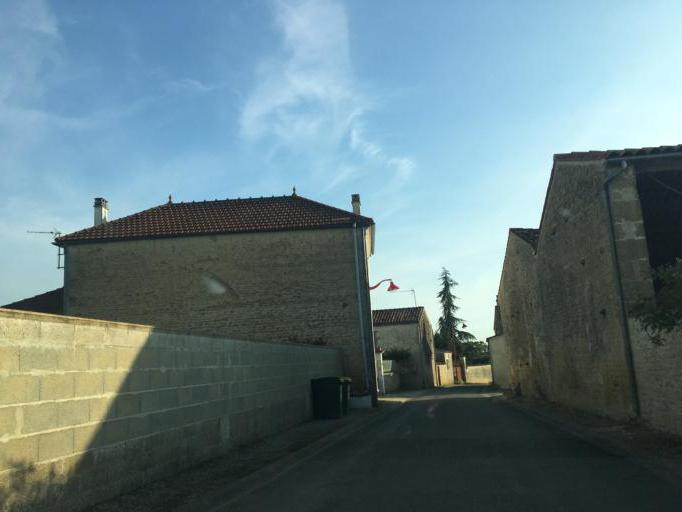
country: FR
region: Poitou-Charentes
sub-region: Departement de la Charente-Maritime
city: Saint-Jean-d'Angely
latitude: 46.0639
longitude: -0.5759
